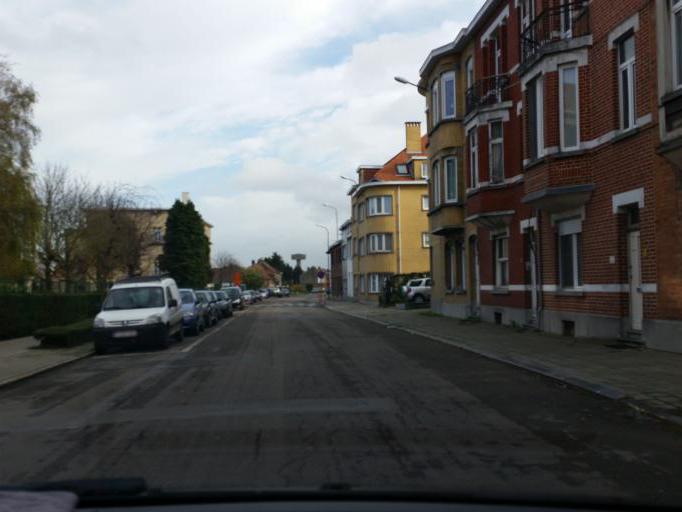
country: BE
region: Flanders
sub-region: Provincie Vlaams-Brabant
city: Grimbergen
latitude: 50.9014
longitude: 4.3649
